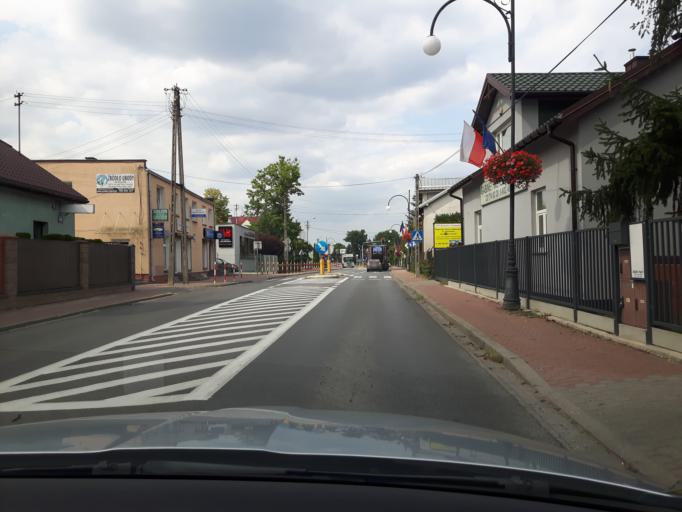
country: PL
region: Masovian Voivodeship
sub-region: Powiat legionowski
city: Nieporet
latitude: 52.4200
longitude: 21.0364
